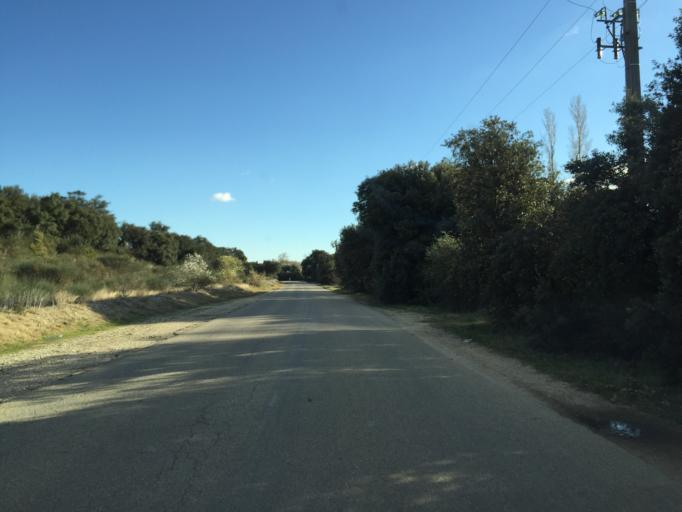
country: FR
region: Provence-Alpes-Cote d'Azur
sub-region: Departement du Vaucluse
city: Sorgues
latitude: 44.0207
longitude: 4.8473
